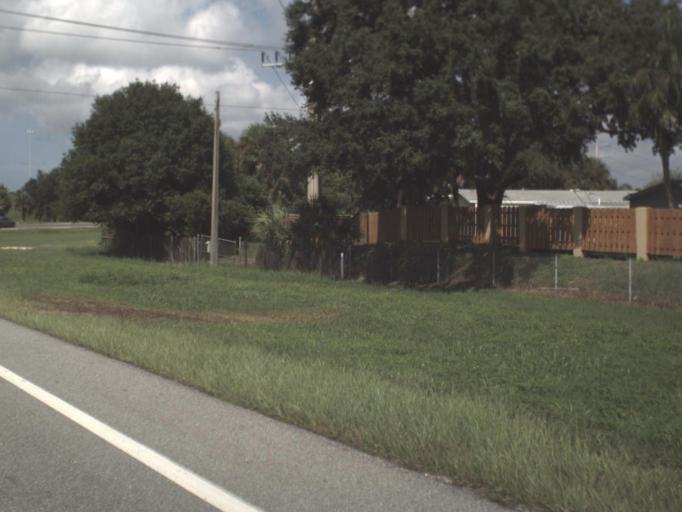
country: US
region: Florida
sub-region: Sarasota County
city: Lake Sarasota
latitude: 27.2696
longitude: -82.4463
